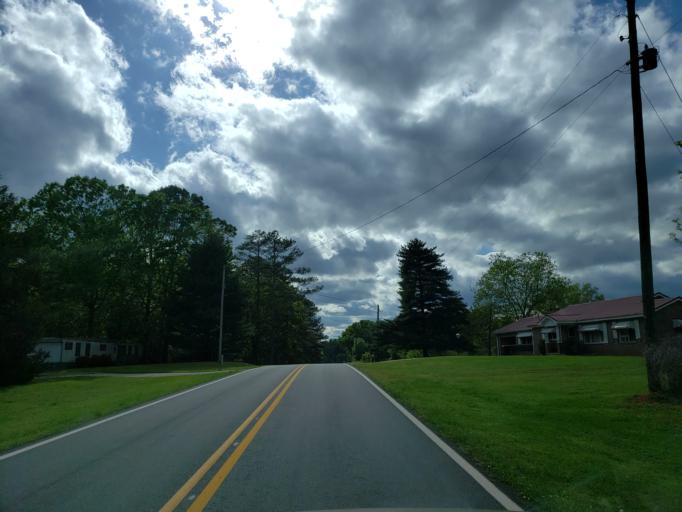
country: US
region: Georgia
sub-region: Carroll County
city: Mount Zion
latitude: 33.6803
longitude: -85.2107
